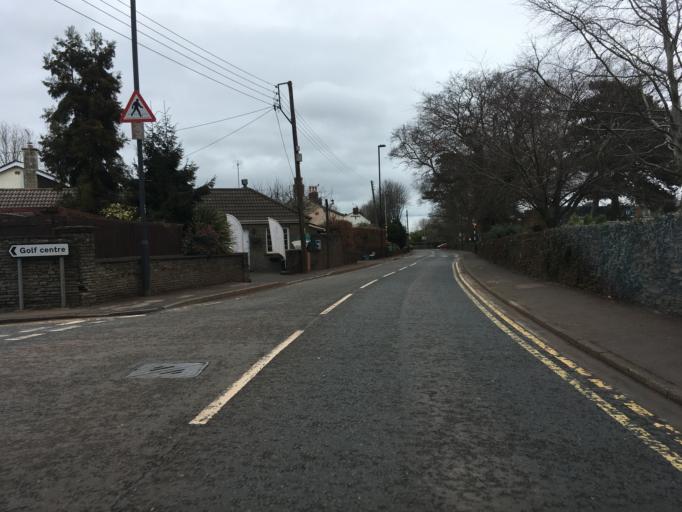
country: GB
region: England
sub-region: South Gloucestershire
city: Stoke Gifford
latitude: 51.5022
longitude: -2.5227
